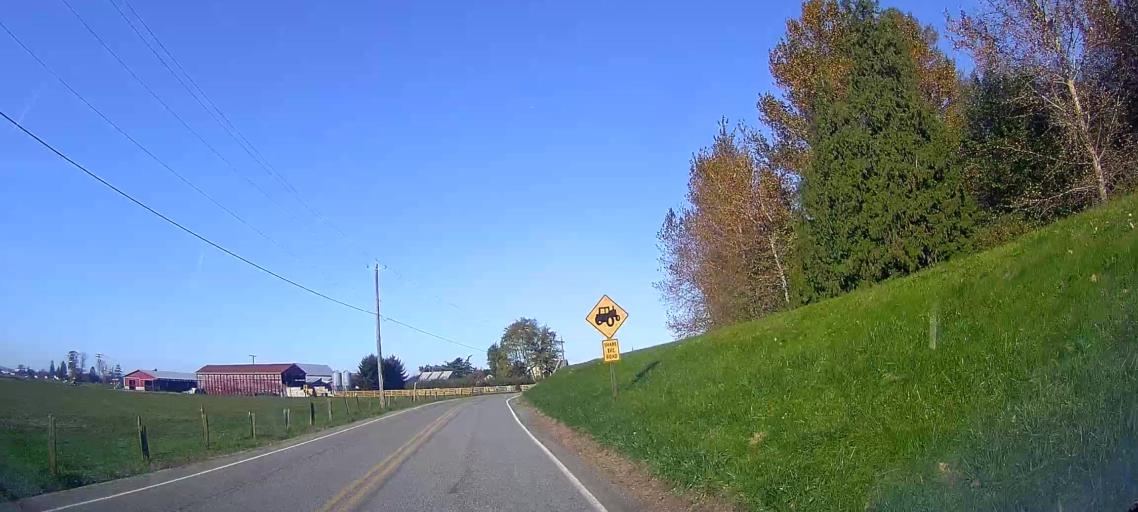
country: US
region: Washington
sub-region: Skagit County
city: Mount Vernon
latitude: 48.4019
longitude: -122.3680
